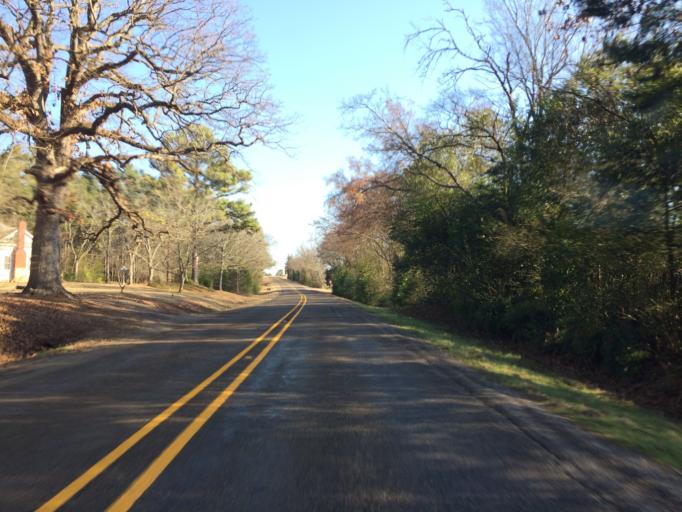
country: US
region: Texas
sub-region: Wood County
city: Quitman
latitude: 32.7041
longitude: -95.3552
